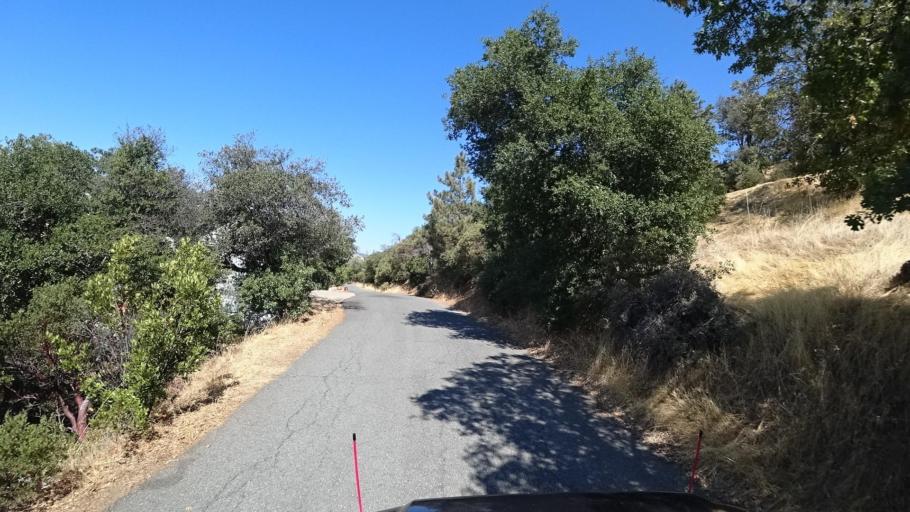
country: US
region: California
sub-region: San Diego County
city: Julian
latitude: 33.0824
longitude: -116.5885
